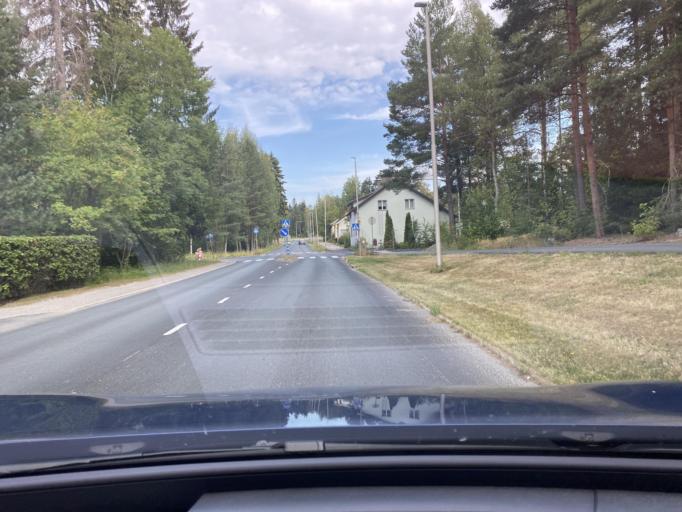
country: FI
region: Pirkanmaa
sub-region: Lounais-Pirkanmaa
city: Vammala
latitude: 61.3530
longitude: 22.8948
